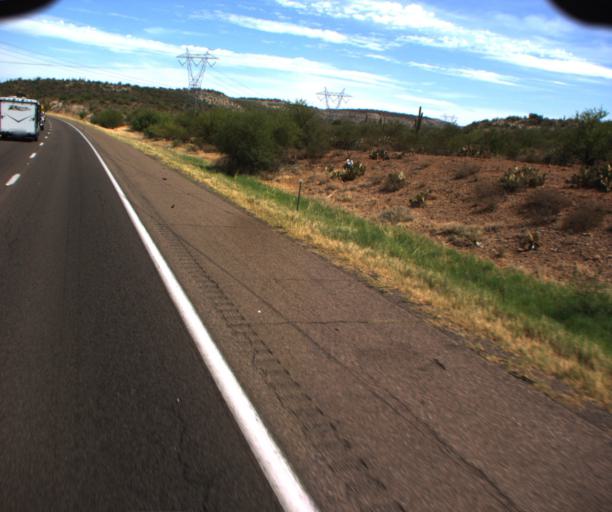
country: US
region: Arizona
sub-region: Yavapai County
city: Black Canyon City
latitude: 34.0074
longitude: -112.1345
